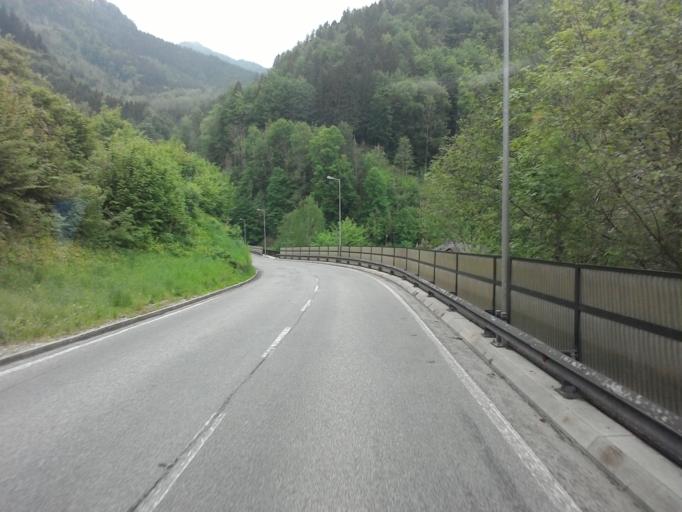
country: AT
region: Styria
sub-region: Politischer Bezirk Liezen
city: Landl
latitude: 47.6657
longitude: 14.7138
